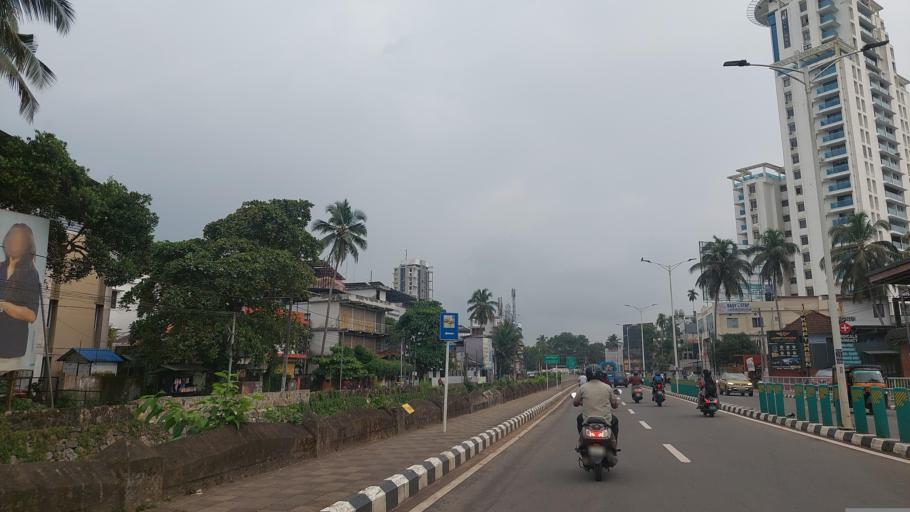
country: IN
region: Kerala
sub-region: Kozhikode
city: Kozhikode
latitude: 11.2816
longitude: 75.7840
